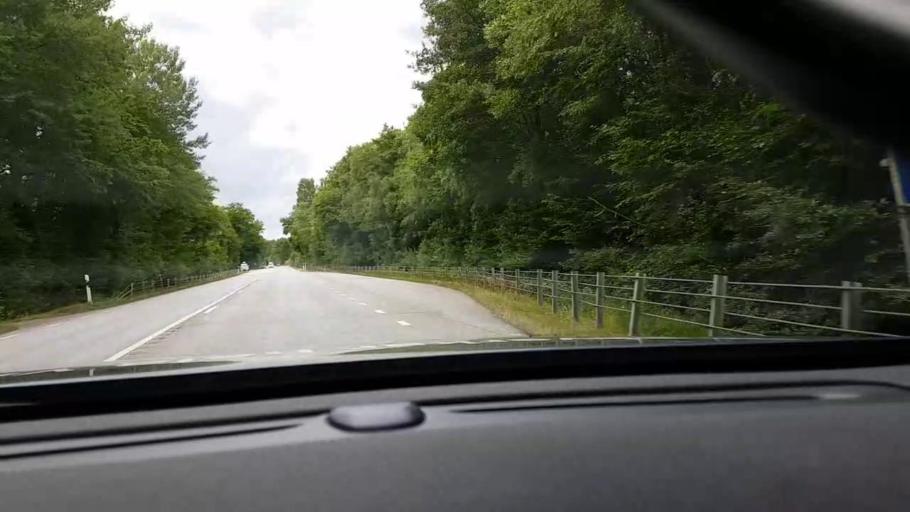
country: SE
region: Skane
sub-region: Horby Kommun
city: Hoerby
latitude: 55.8820
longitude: 13.6314
